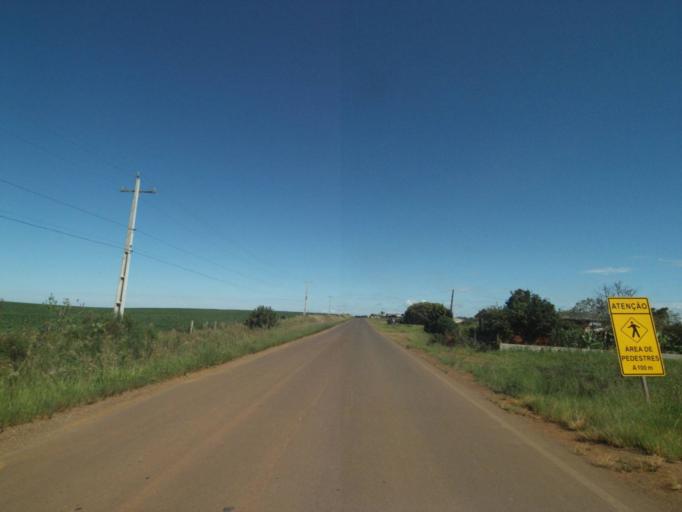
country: BR
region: Parana
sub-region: Pinhao
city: Pinhao
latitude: -25.8298
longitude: -52.0350
